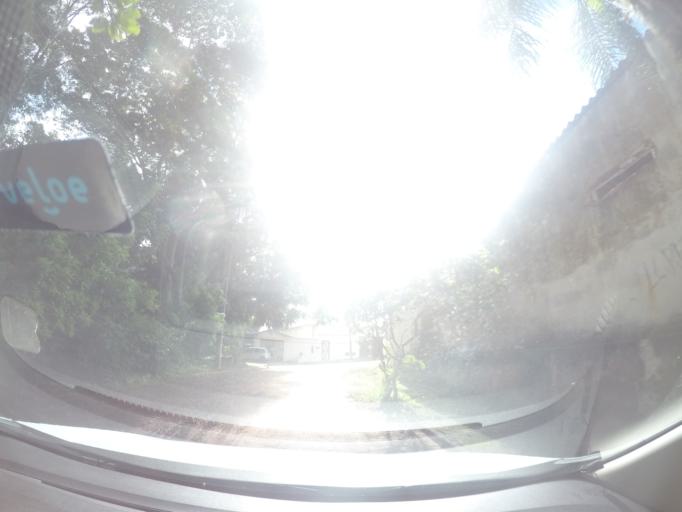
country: BR
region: Goias
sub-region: Goiania
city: Goiania
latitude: -16.6917
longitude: -49.2011
